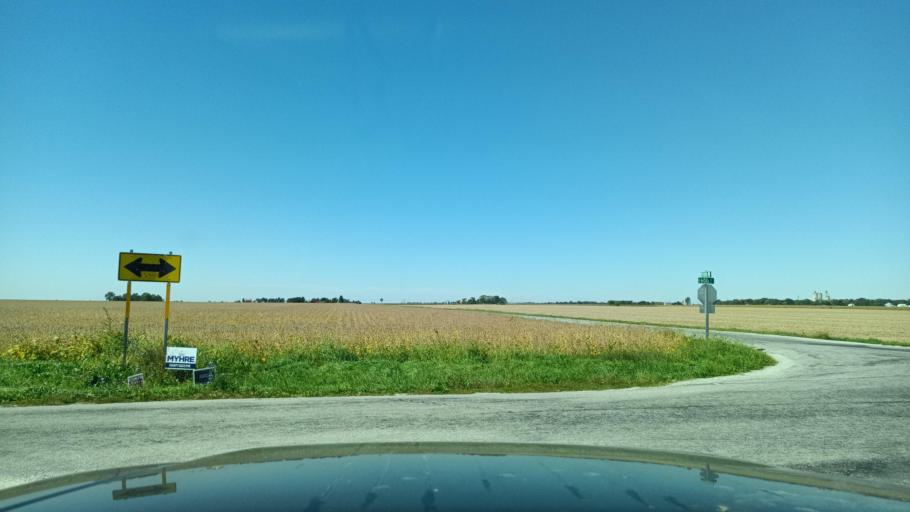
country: US
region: Illinois
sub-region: Champaign County
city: Savoy
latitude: 40.0986
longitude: -88.3505
